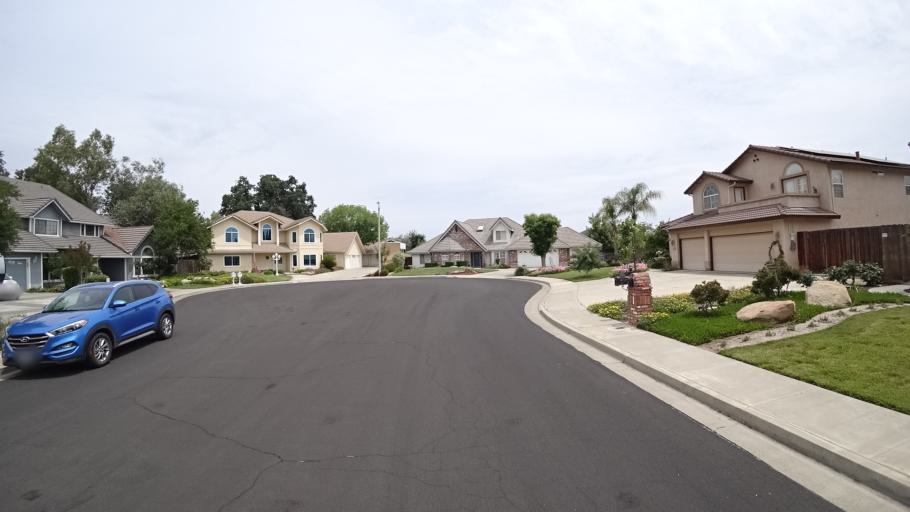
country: US
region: California
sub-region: Kings County
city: Lucerne
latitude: 36.3561
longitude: -119.6535
